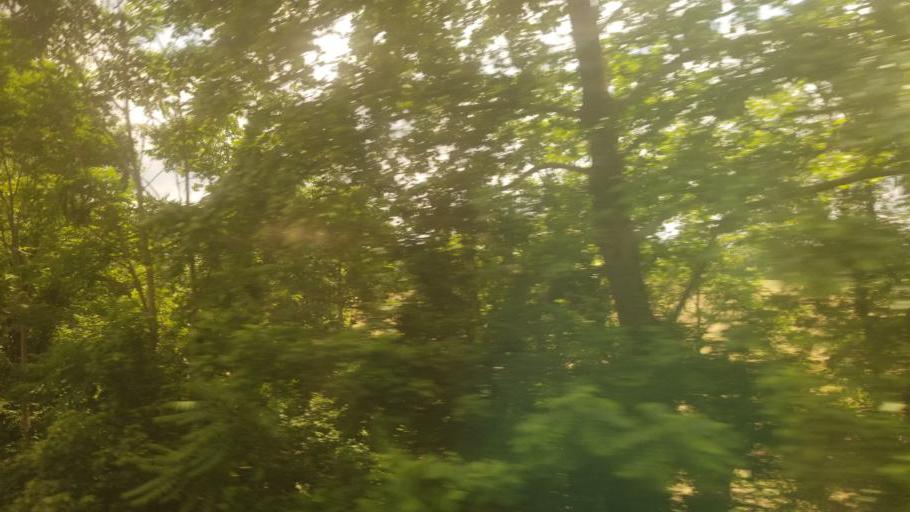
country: US
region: Maryland
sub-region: Montgomery County
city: Poolesville
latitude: 39.2200
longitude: -77.4104
